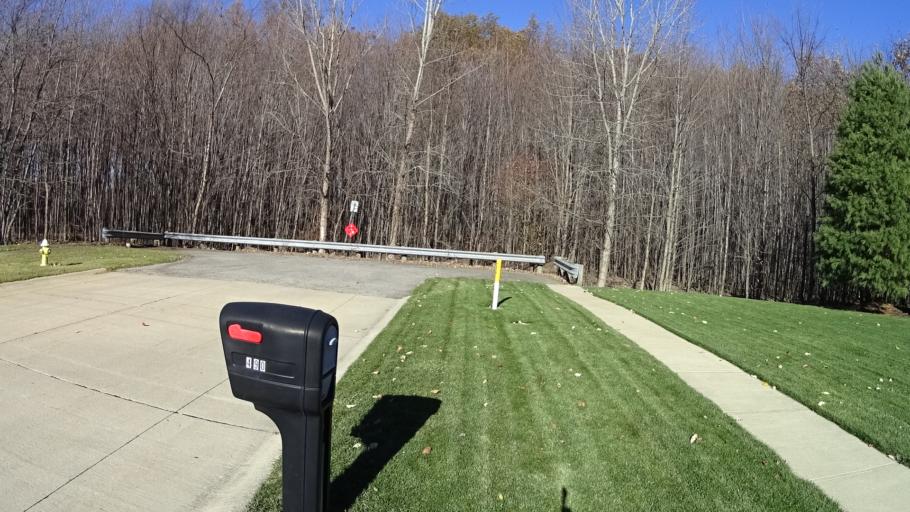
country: US
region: Ohio
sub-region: Lorain County
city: Elyria
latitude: 41.3517
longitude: -82.0629
